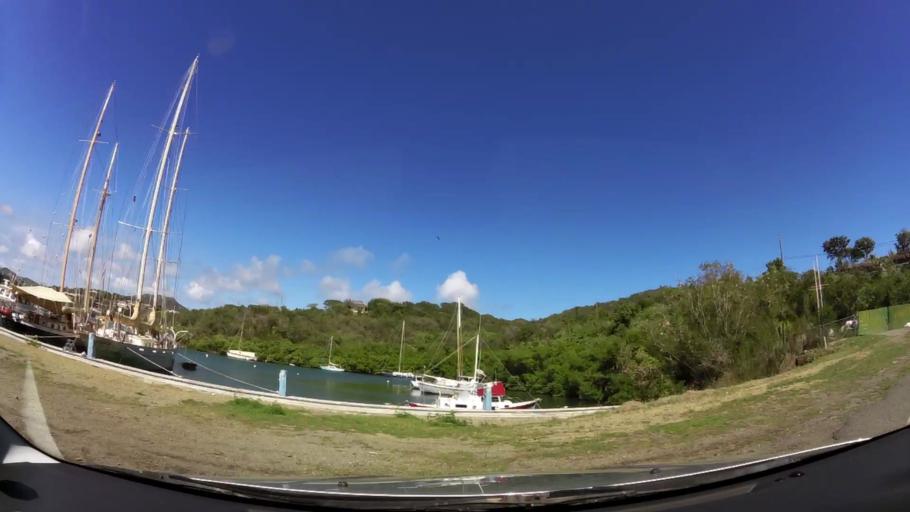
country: AG
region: Saint Paul
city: Falmouth
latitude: 17.0076
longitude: -61.7620
